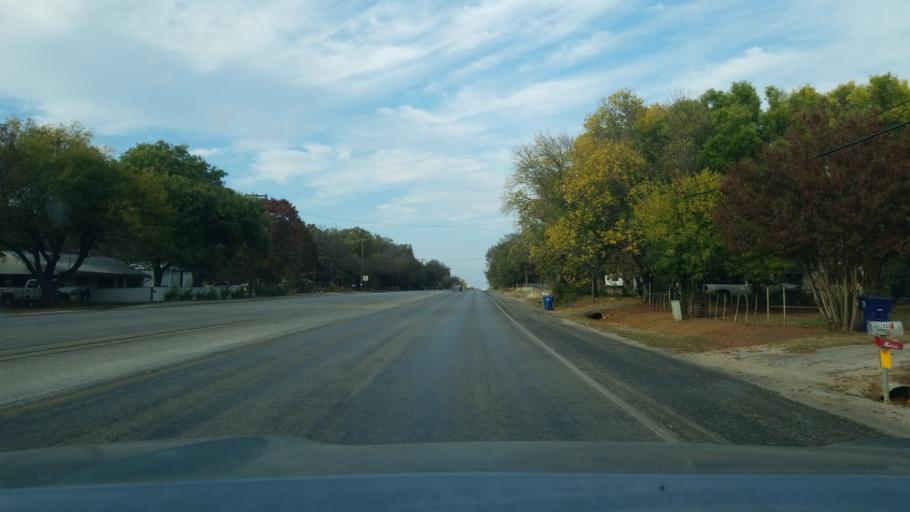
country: US
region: Texas
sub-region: Brown County
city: Early
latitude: 31.7478
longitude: -98.9639
